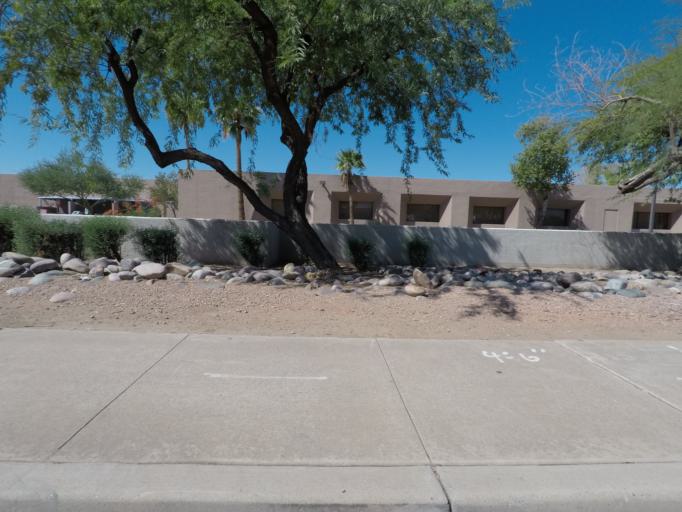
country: US
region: Arizona
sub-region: Maricopa County
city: Tempe Junction
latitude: 33.4067
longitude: -111.9479
